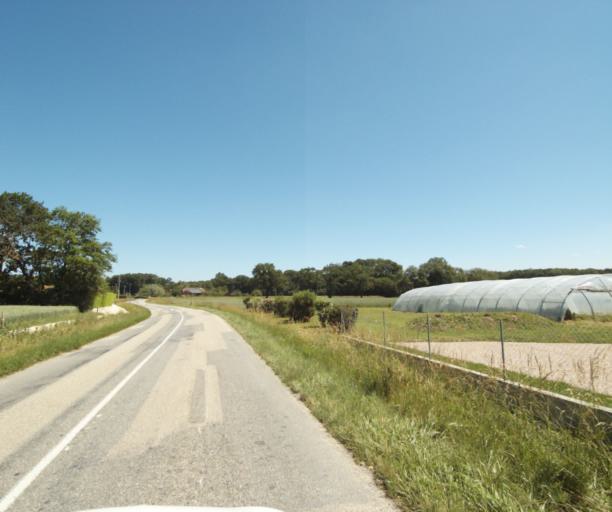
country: FR
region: Rhone-Alpes
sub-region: Departement de la Haute-Savoie
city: Veigy-Foncenex
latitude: 46.2783
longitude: 6.2599
